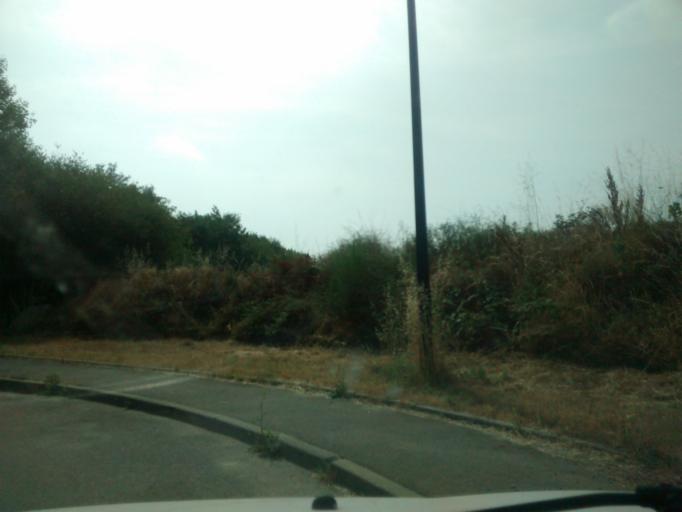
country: FR
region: Brittany
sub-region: Departement d'Ille-et-Vilaine
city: Saint-Jacques-de-la-Lande
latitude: 48.0737
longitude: -1.7220
